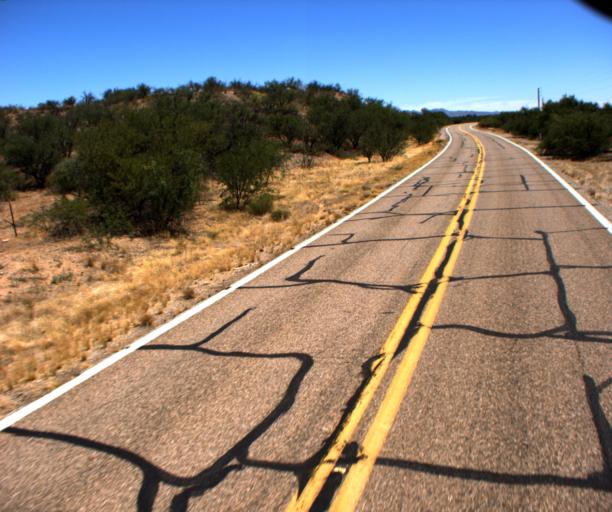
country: US
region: Arizona
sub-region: Pima County
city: Three Points
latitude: 31.8466
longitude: -111.3989
